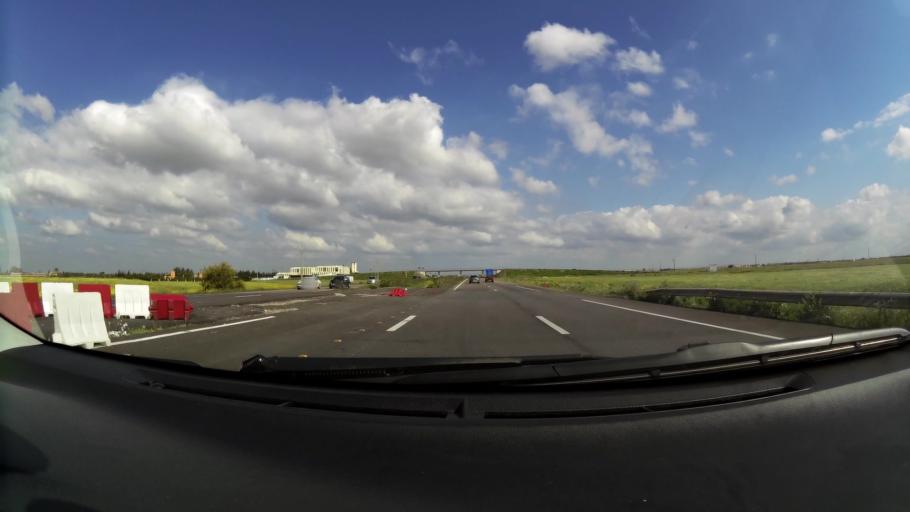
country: MA
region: Chaouia-Ouardigha
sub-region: Settat Province
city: Berrechid
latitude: 33.3140
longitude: -7.5976
